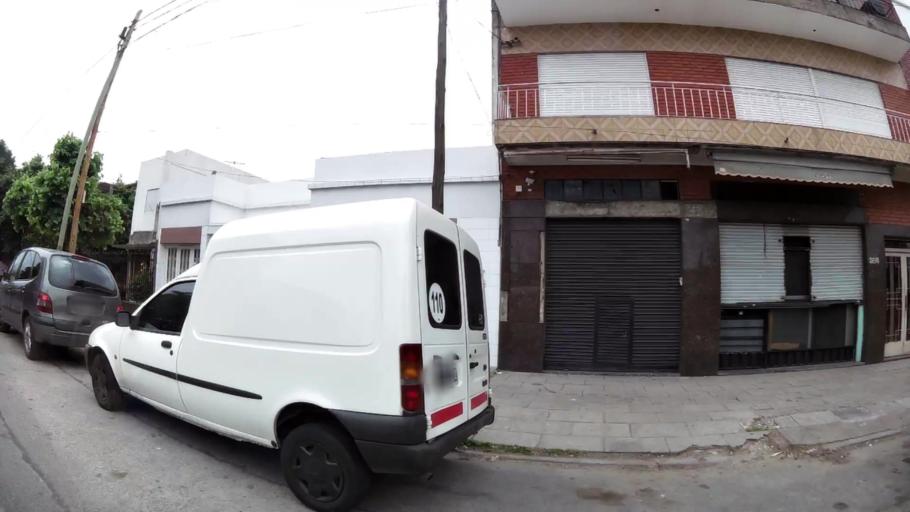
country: AR
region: Buenos Aires
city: San Justo
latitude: -34.6646
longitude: -58.5213
